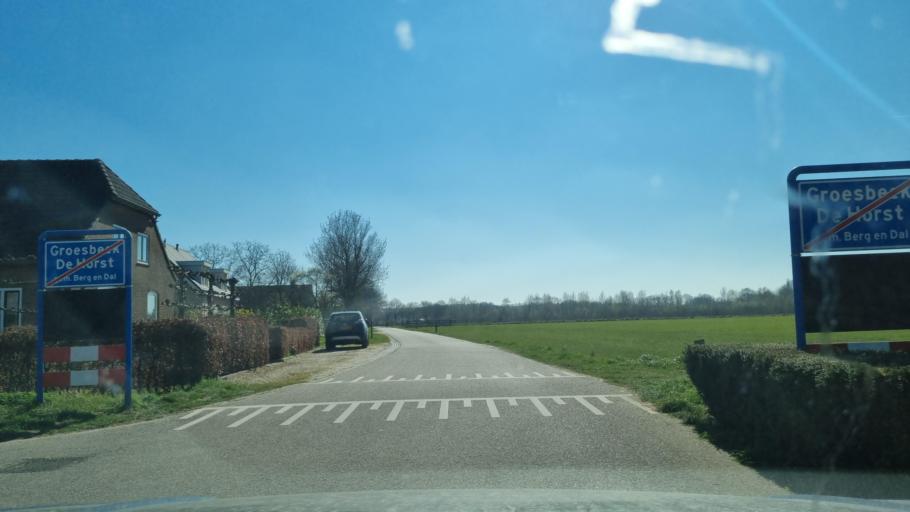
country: NL
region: Gelderland
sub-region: Gemeente Groesbeek
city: De Horst
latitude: 51.7724
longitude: 5.9693
